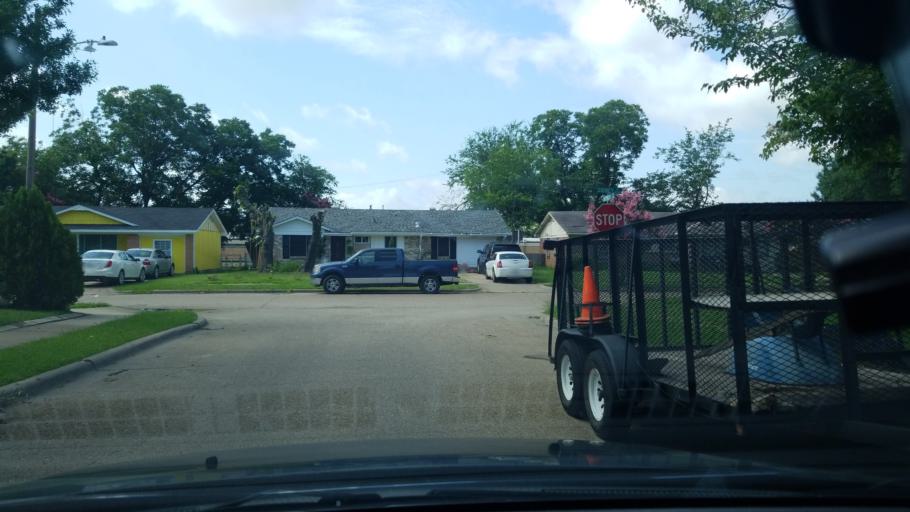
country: US
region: Texas
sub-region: Dallas County
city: Mesquite
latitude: 32.8200
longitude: -96.6545
